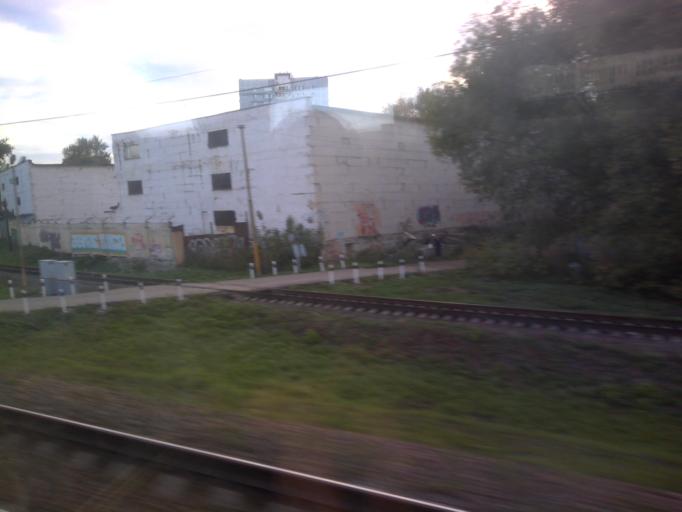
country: RU
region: Moscow
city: Novyye Cheremushki
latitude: 55.6927
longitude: 37.6161
